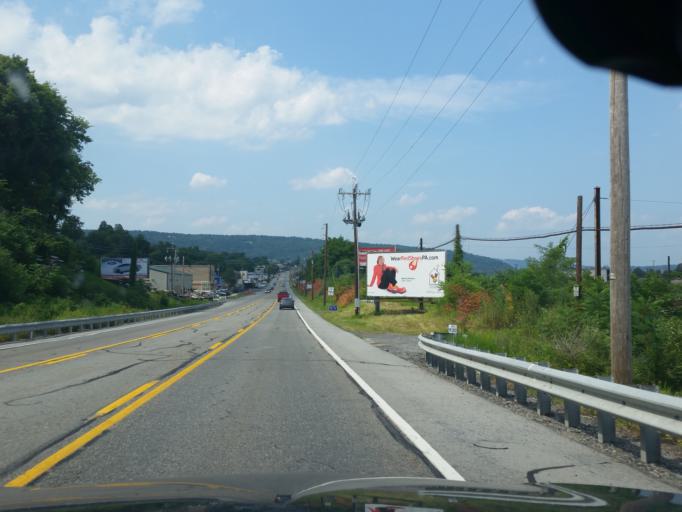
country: US
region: Pennsylvania
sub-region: Cumberland County
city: Enola
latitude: 40.2864
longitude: -76.9296
